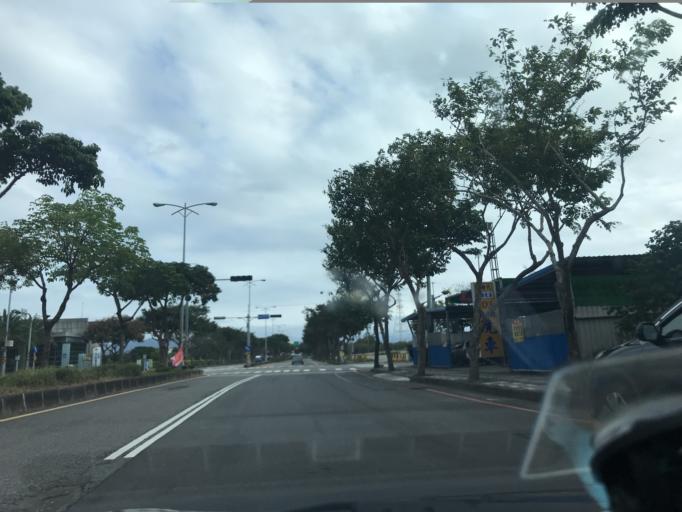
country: TW
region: Taiwan
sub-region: Hsinchu
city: Zhubei
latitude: 24.8047
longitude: 121.0433
